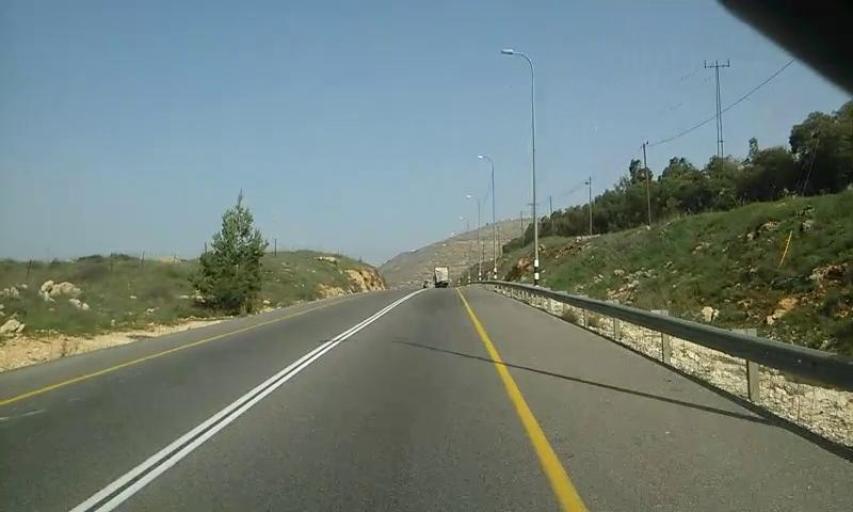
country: PS
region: West Bank
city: Qaryut
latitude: 32.0562
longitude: 35.2862
